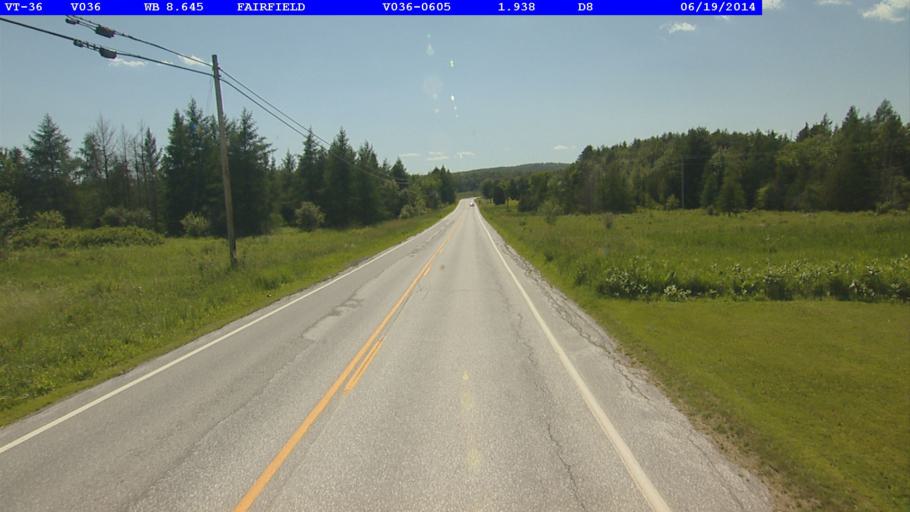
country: US
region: Vermont
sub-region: Franklin County
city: Saint Albans
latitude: 44.7885
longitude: -72.9931
